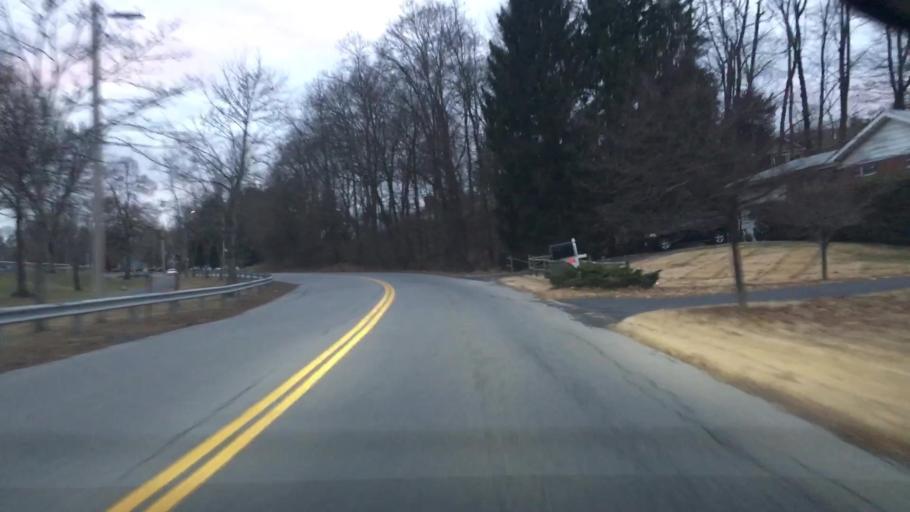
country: US
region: New York
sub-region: Dutchess County
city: Spackenkill
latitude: 41.6776
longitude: -73.9116
